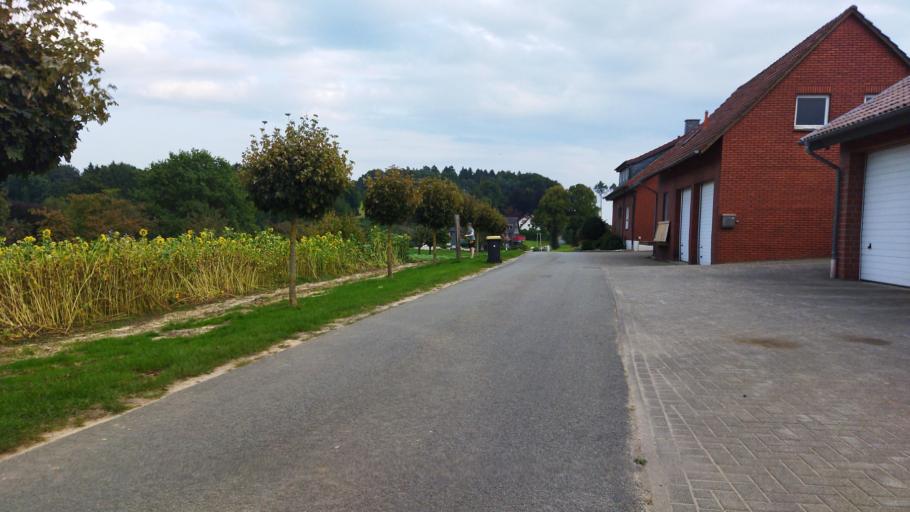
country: DE
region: Lower Saxony
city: Bad Iburg
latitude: 52.1734
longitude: 8.0149
